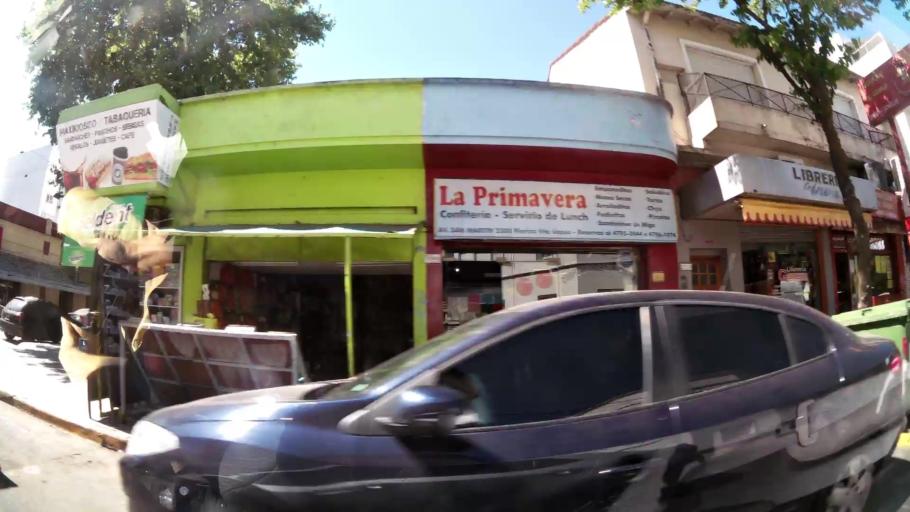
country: AR
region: Buenos Aires
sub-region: Partido de Vicente Lopez
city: Olivos
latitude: -34.5288
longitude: -58.4936
